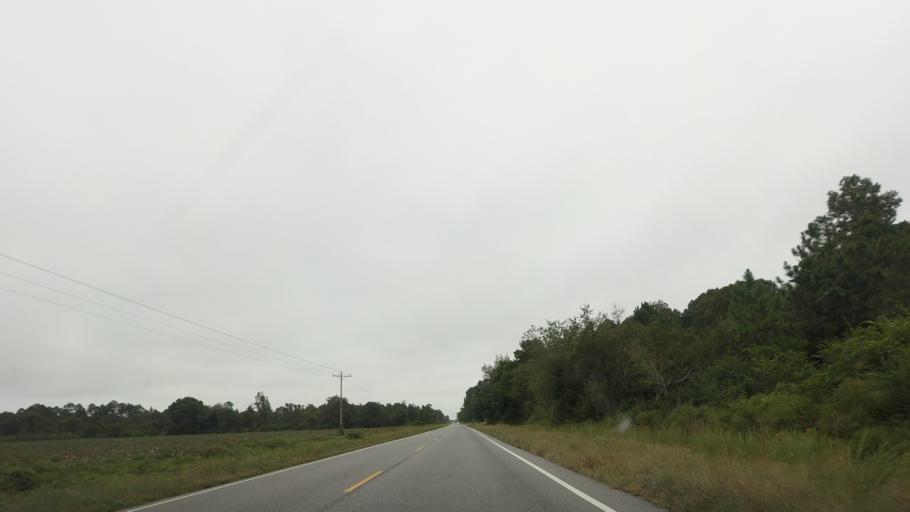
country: US
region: Georgia
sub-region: Berrien County
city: Enigma
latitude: 31.3349
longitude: -83.2295
